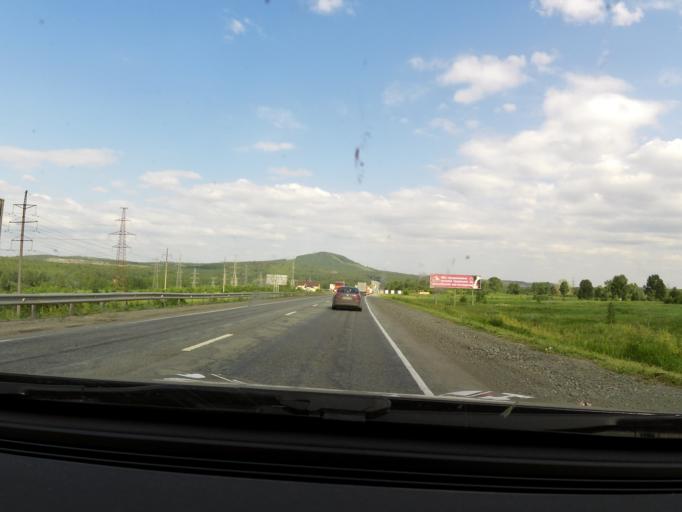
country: RU
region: Sverdlovsk
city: Revda
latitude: 56.8277
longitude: 59.9486
